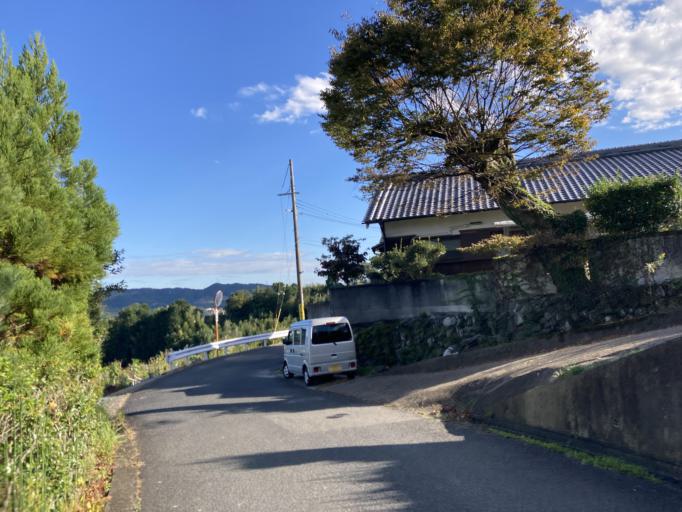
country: JP
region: Nara
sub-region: Ikoma-shi
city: Ikoma
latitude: 34.6699
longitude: 135.6936
